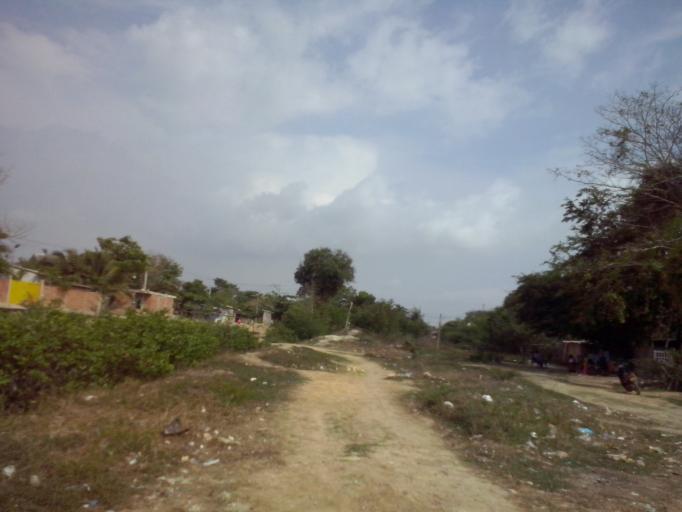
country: CO
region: Bolivar
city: Cartagena
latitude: 10.4148
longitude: -75.4662
